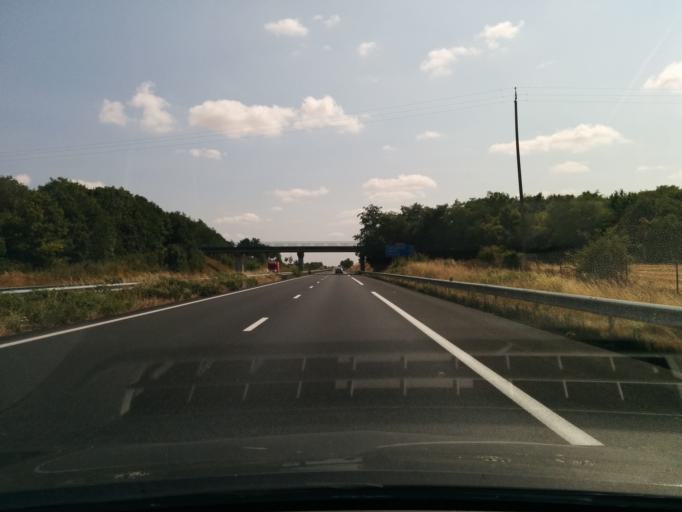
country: FR
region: Centre
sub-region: Departement de l'Indre
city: Vatan
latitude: 47.0394
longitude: 1.7942
